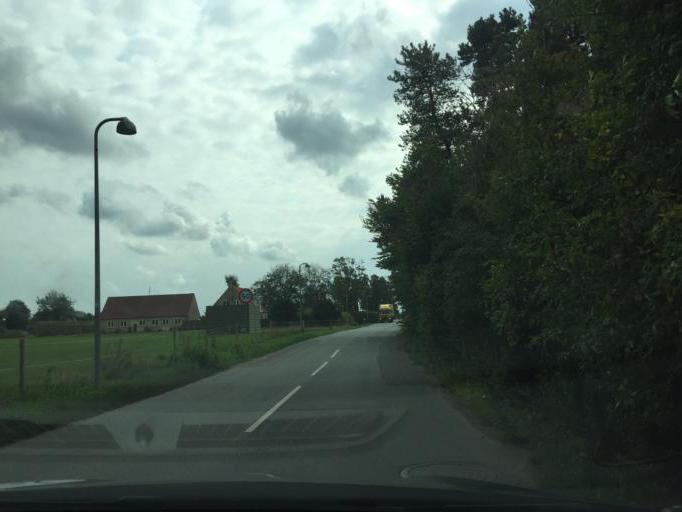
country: DK
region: South Denmark
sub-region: Odense Kommune
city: Stige
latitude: 55.4459
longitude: 10.4014
